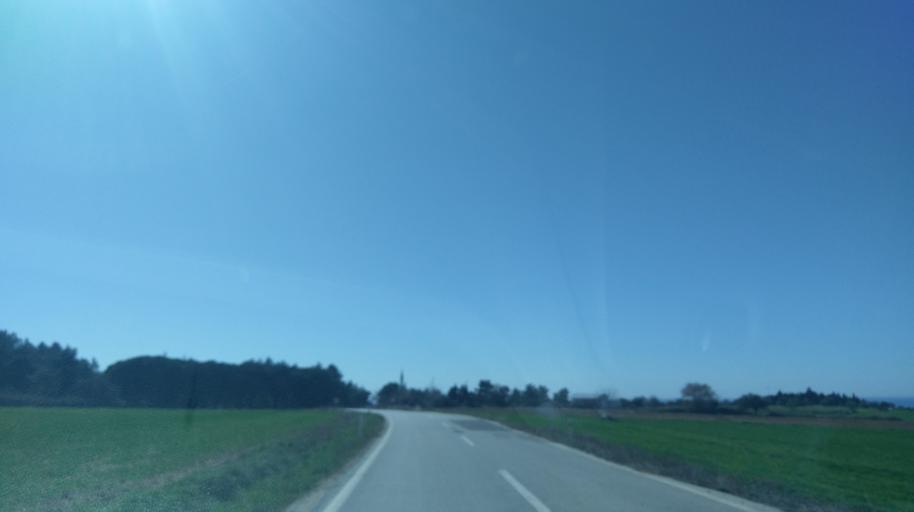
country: TR
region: Canakkale
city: Intepe
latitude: 40.1010
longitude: 26.2293
